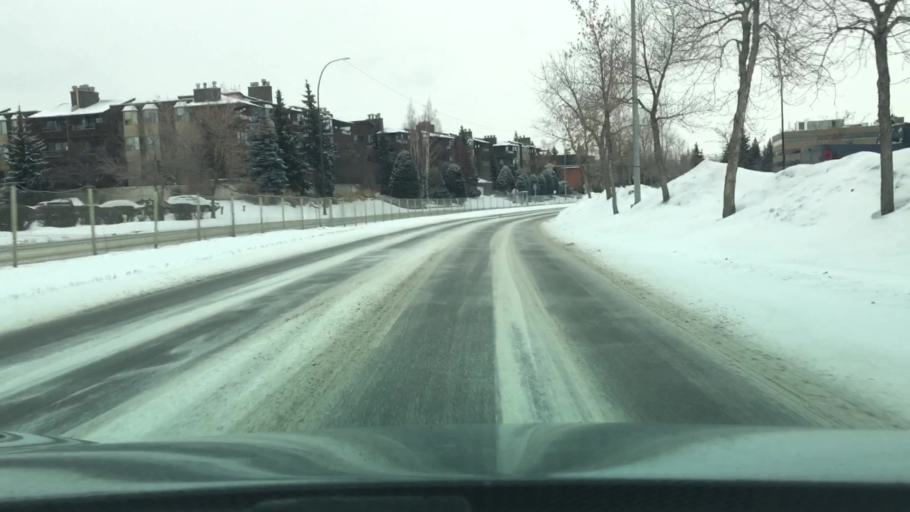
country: CA
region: Alberta
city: Calgary
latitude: 51.0849
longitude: -114.1588
